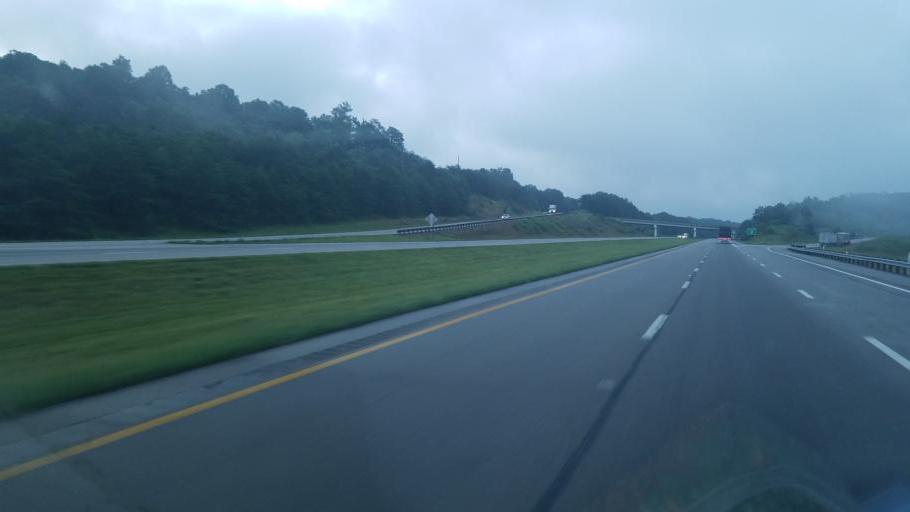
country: US
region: Ohio
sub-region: Jackson County
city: Jackson
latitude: 39.0970
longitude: -82.6642
